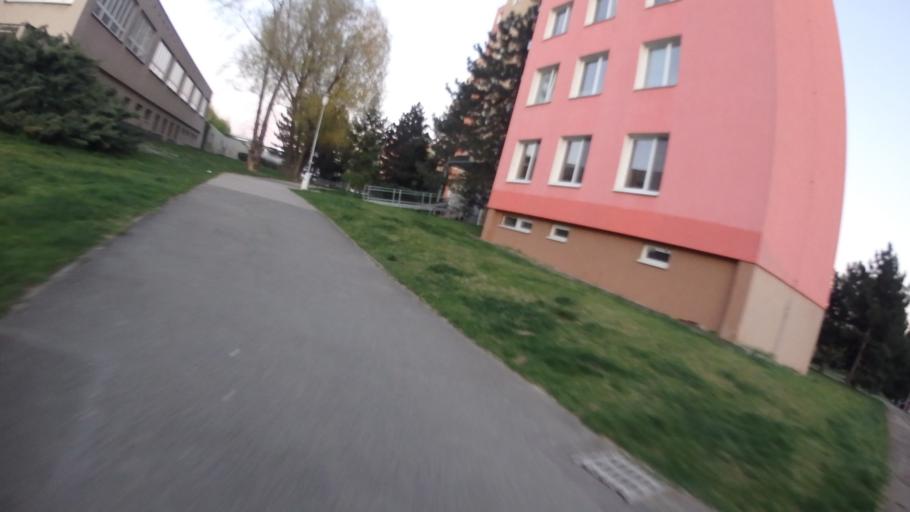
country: CZ
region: South Moravian
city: Ostopovice
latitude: 49.1678
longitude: 16.5634
